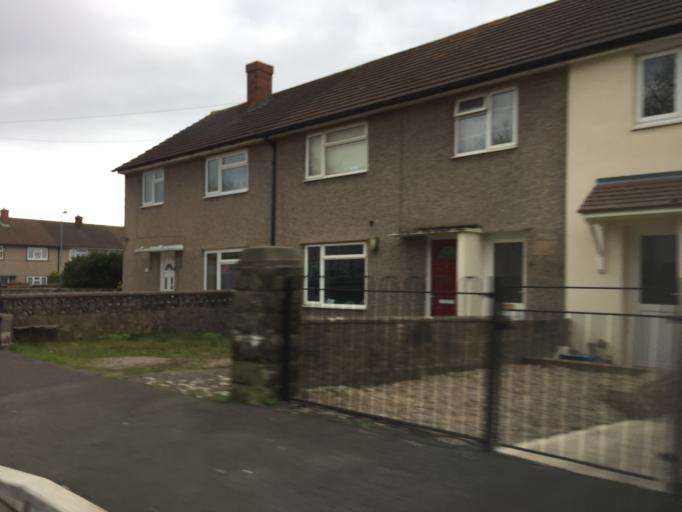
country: GB
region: Wales
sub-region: Monmouthshire
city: Chepstow
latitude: 51.6307
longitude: -2.6788
